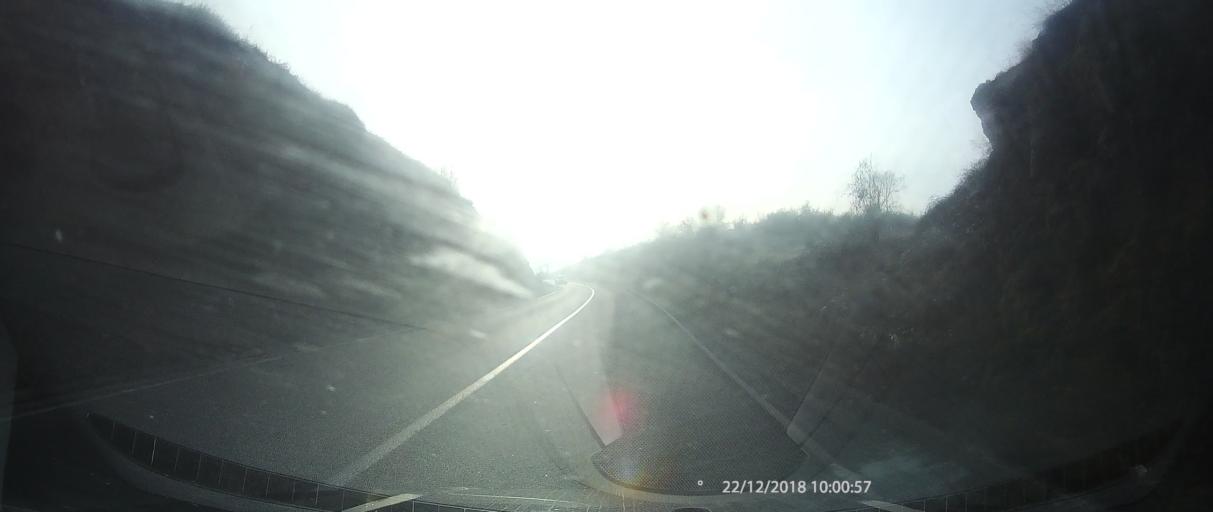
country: MK
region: Opstina Rankovce
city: Rankovce
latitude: 42.1469
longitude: 21.9883
